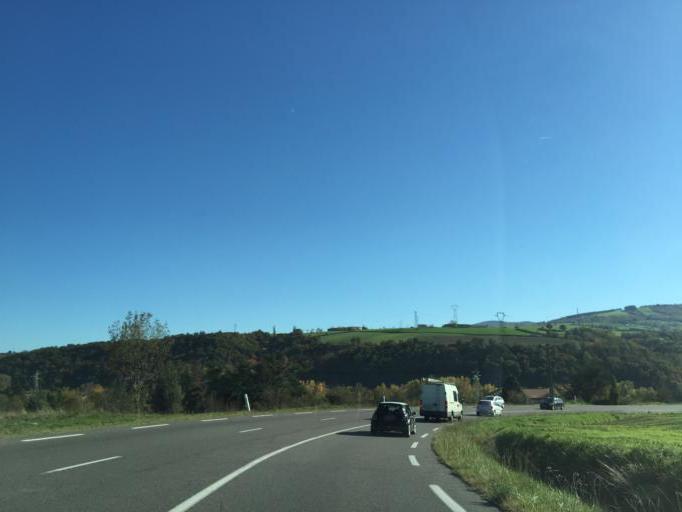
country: FR
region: Rhone-Alpes
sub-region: Departement de la Loire
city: Chateauneuf
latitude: 45.5449
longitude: 4.6474
